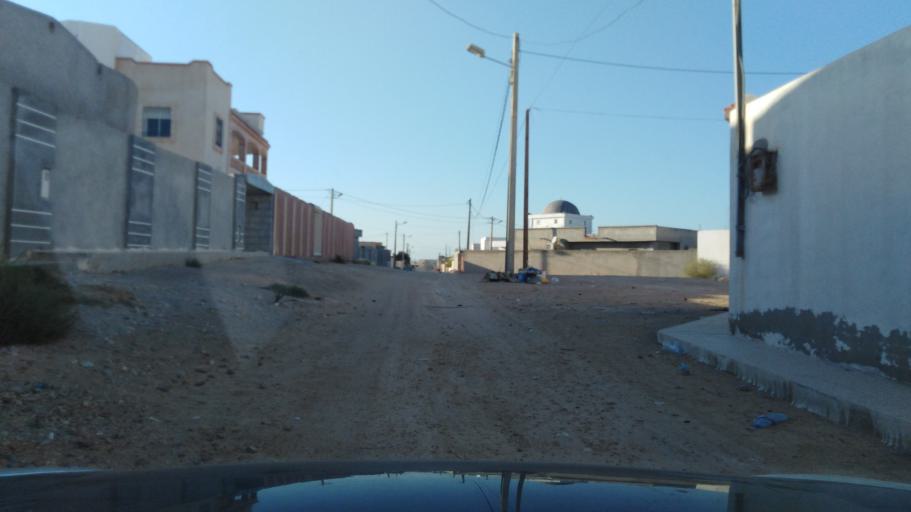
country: TN
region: Qabis
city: Gabes
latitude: 33.9507
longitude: 10.0132
